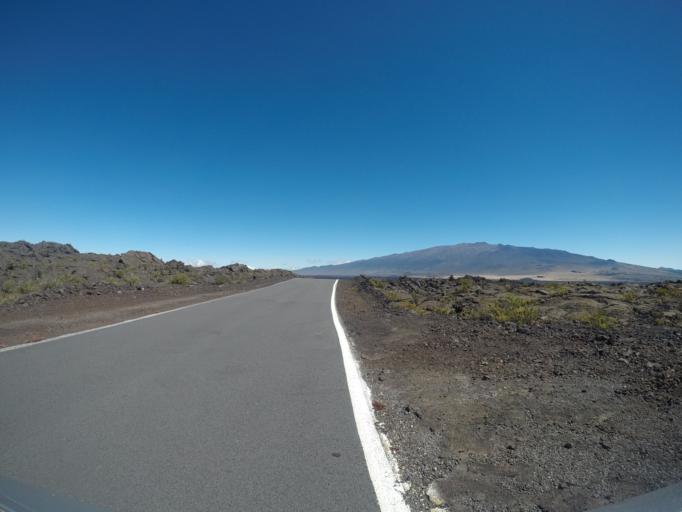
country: US
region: Hawaii
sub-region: Hawaii County
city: Volcano
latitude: 19.6282
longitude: -155.4782
